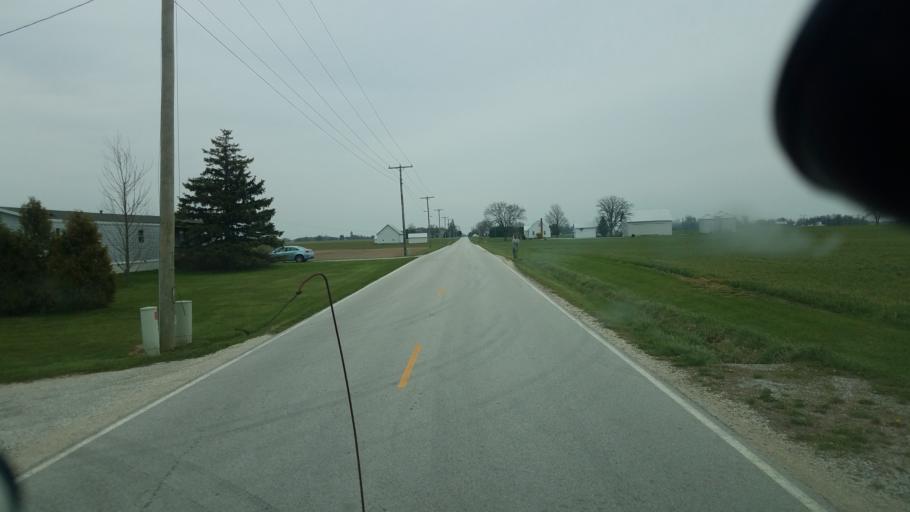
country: US
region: Ohio
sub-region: Wyandot County
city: Carey
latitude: 41.0505
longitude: -83.3510
